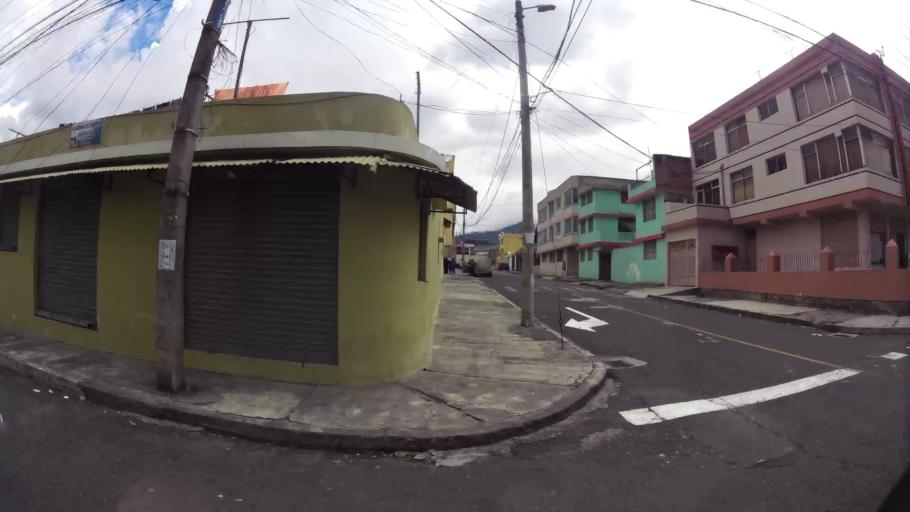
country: EC
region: Pichincha
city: Quito
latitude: -0.2498
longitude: -78.5278
